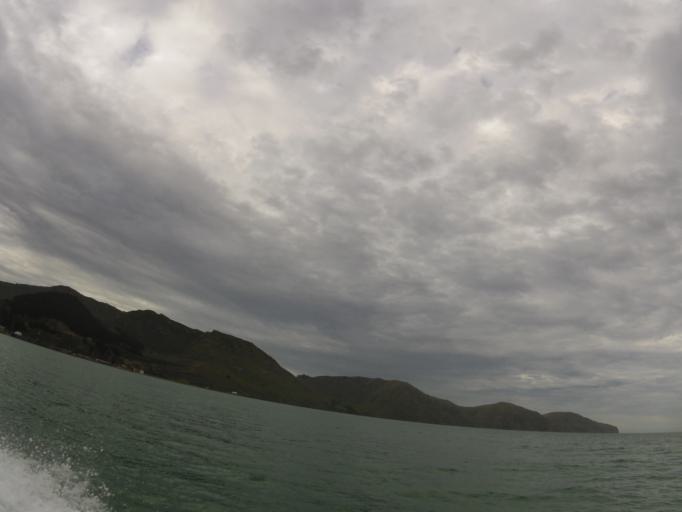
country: NZ
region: Canterbury
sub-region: Christchurch City
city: Christchurch
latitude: -43.6222
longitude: 172.7345
